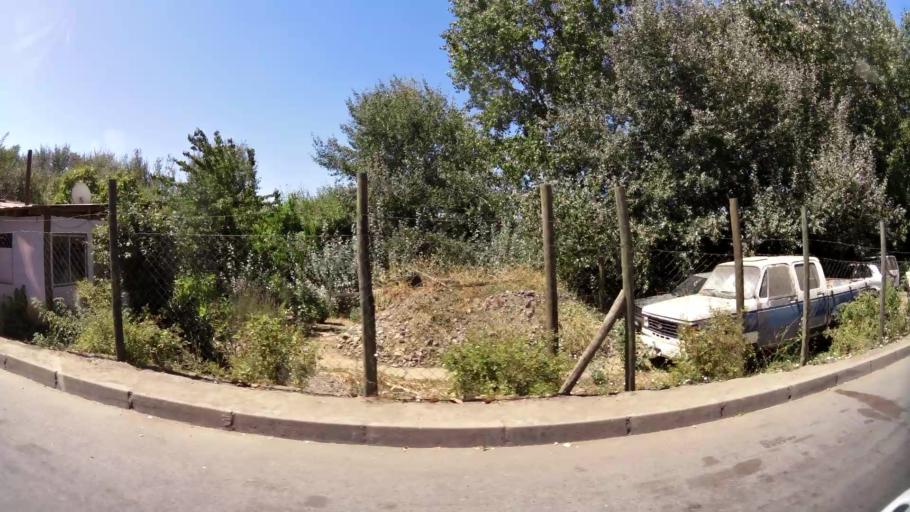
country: CL
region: Maule
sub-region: Provincia de Talca
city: Talca
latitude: -35.3036
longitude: -71.5160
